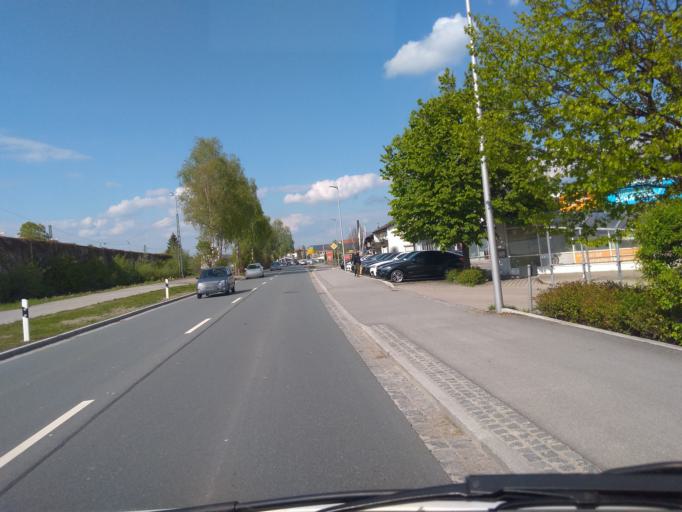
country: DE
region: Bavaria
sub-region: Upper Bavaria
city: Raubling
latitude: 47.7883
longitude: 12.1106
